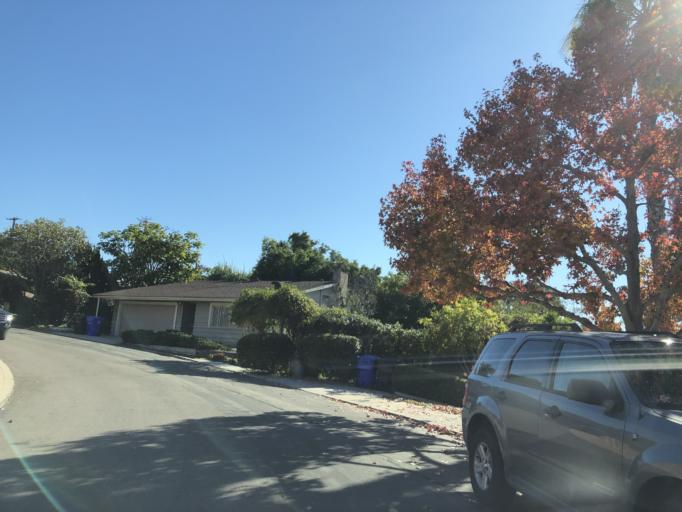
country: US
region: California
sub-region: San Diego County
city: San Diego
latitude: 32.7310
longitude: -117.1326
